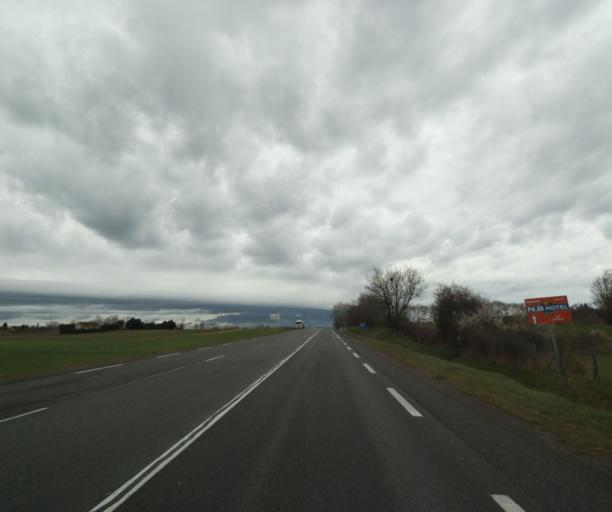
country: FR
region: Auvergne
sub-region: Departement de l'Allier
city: Toulon-sur-Allier
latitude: 46.4871
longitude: 3.3654
